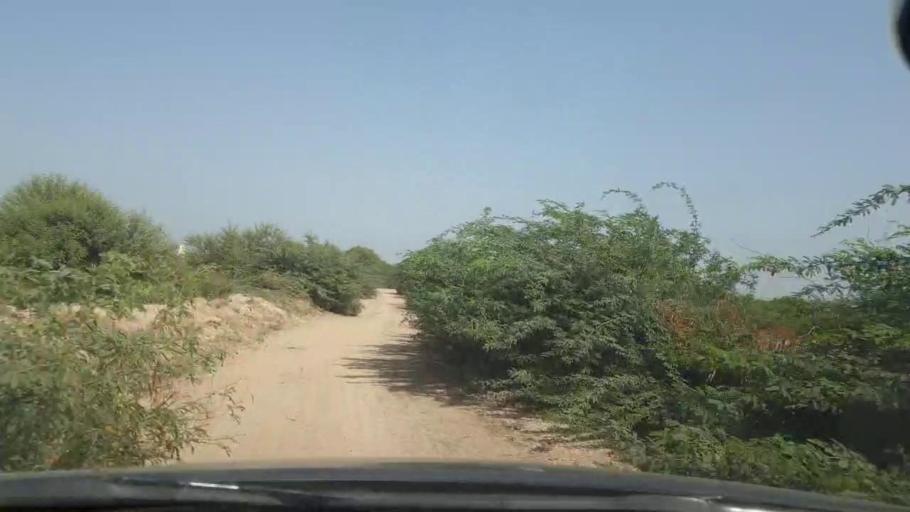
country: PK
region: Sindh
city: Naukot
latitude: 24.8015
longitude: 69.2570
